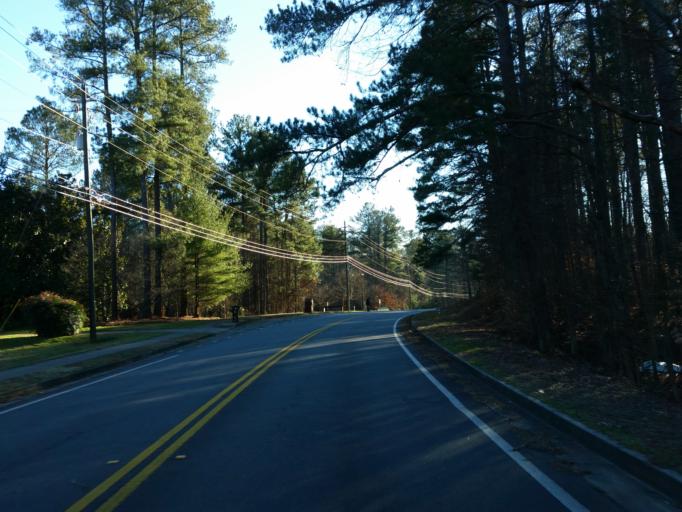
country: US
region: Georgia
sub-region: Cobb County
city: Kennesaw
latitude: 33.9735
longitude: -84.6919
